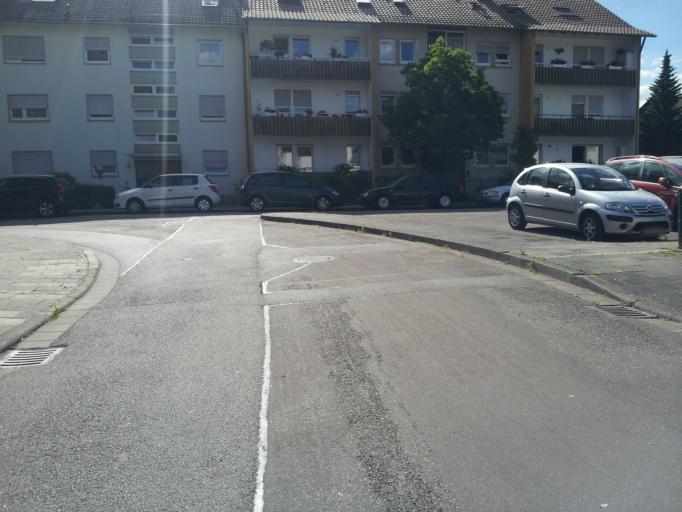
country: DE
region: Baden-Wuerttemberg
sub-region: Karlsruhe Region
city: Heidelberg
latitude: 49.3851
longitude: 8.6685
